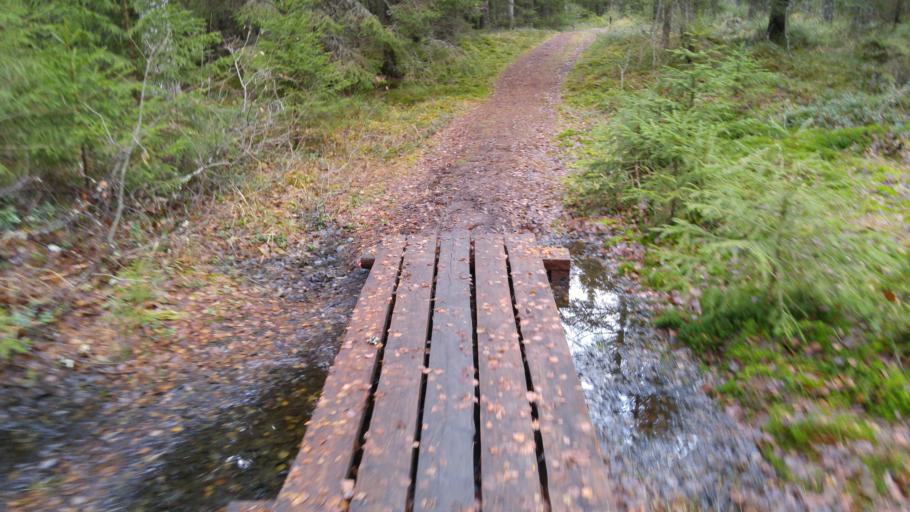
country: FI
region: Pirkanmaa
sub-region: Tampere
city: Kangasala
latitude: 61.6042
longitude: 23.9896
